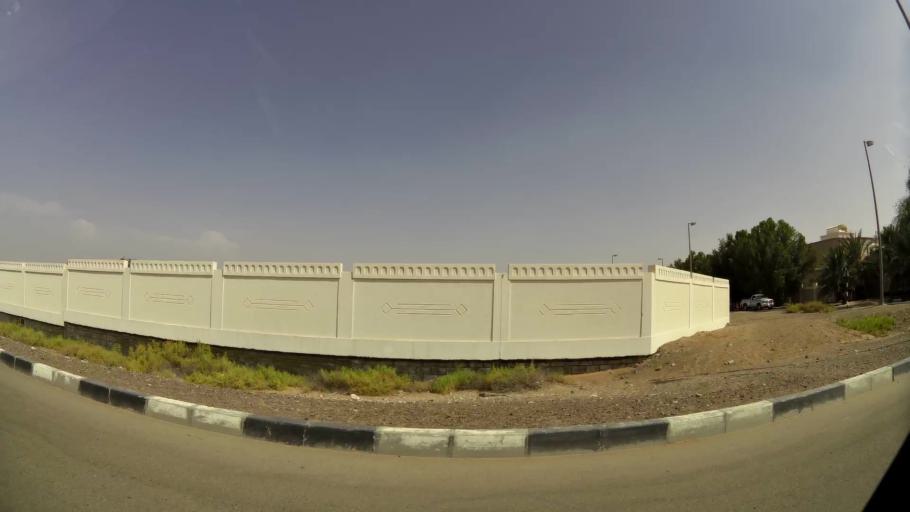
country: AE
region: Abu Dhabi
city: Al Ain
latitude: 24.2337
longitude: 55.6864
